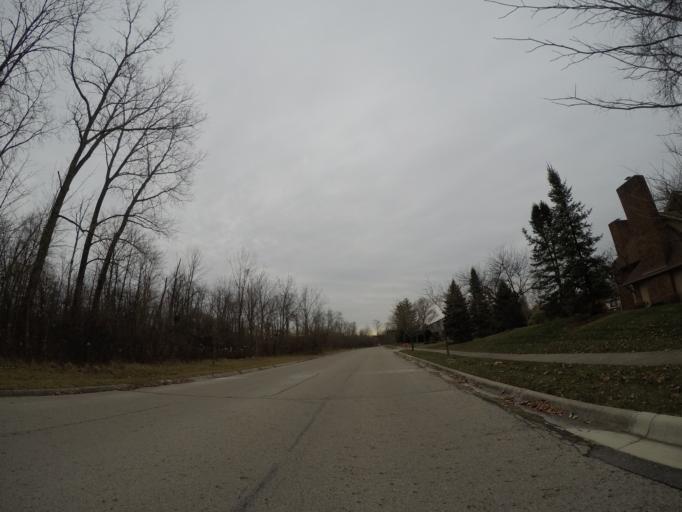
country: US
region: Ohio
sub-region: Franklin County
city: Dublin
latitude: 40.0545
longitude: -83.0855
